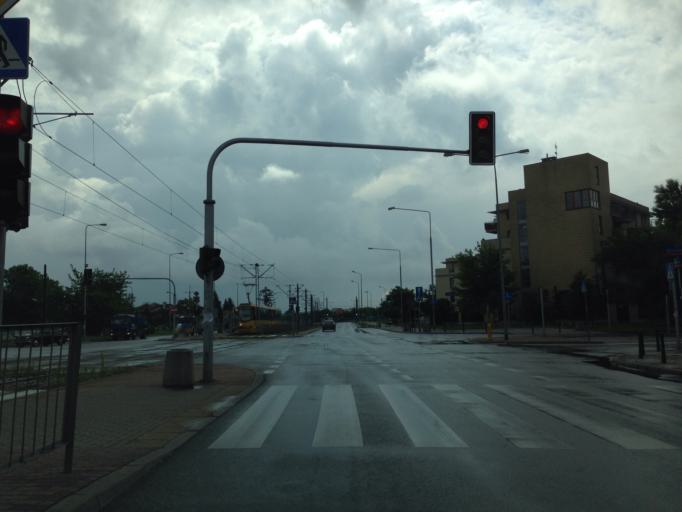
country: PL
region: Masovian Voivodeship
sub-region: Warszawa
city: Bemowo
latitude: 52.2489
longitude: 20.9203
